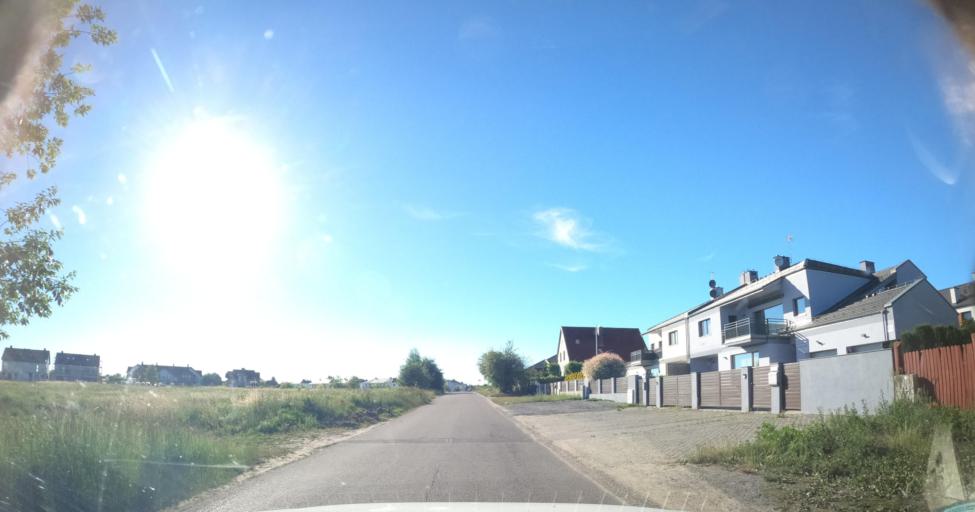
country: PL
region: West Pomeranian Voivodeship
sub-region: Szczecin
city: Szczecin
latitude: 53.4803
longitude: 14.5294
